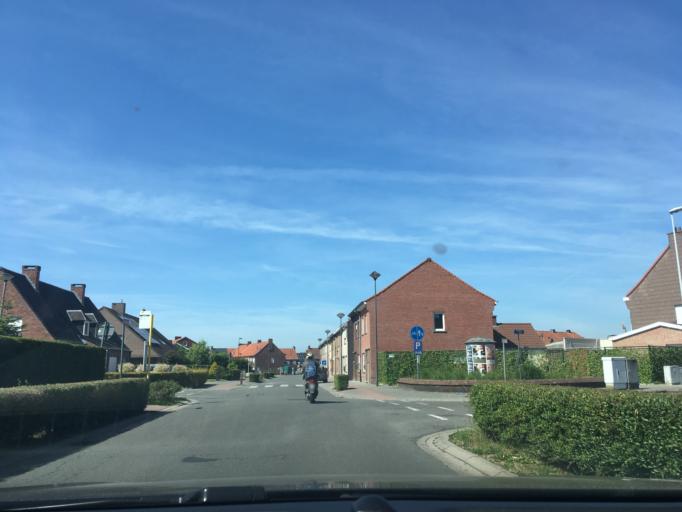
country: BE
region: Flanders
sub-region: Provincie West-Vlaanderen
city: Tielt
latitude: 50.9936
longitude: 3.3155
